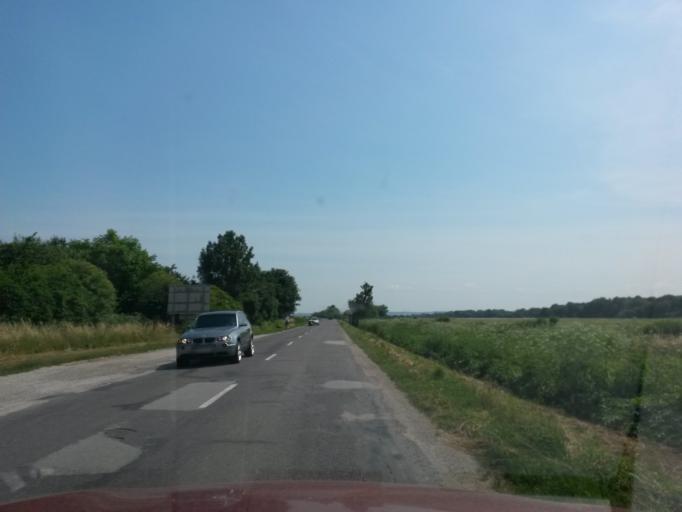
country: SK
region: Kosicky
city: Moldava nad Bodvou
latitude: 48.6496
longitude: 21.0063
